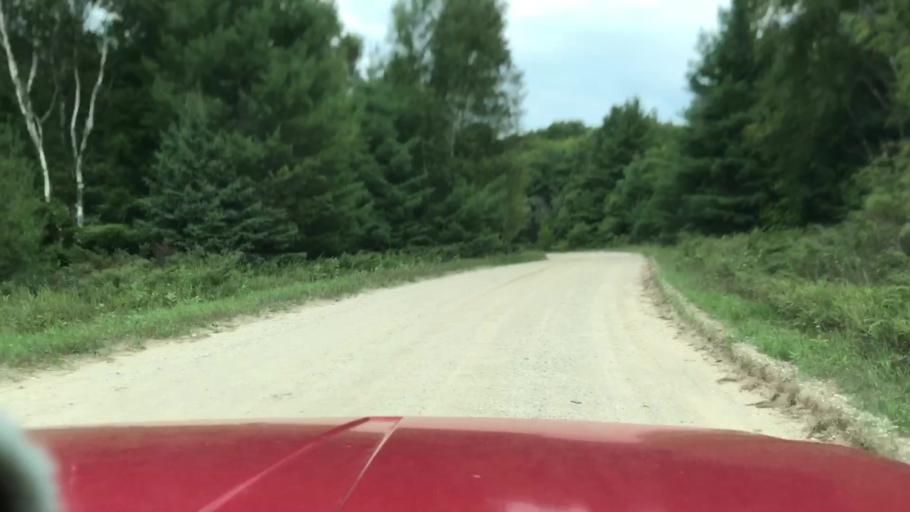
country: US
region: Michigan
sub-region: Charlevoix County
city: Charlevoix
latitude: 45.7210
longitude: -85.5618
